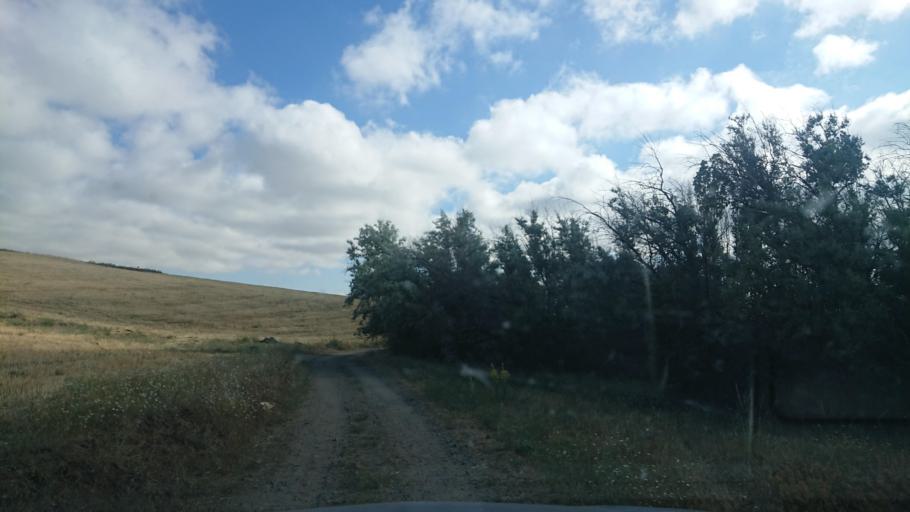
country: TR
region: Aksaray
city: Agacoren
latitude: 38.8563
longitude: 33.9340
